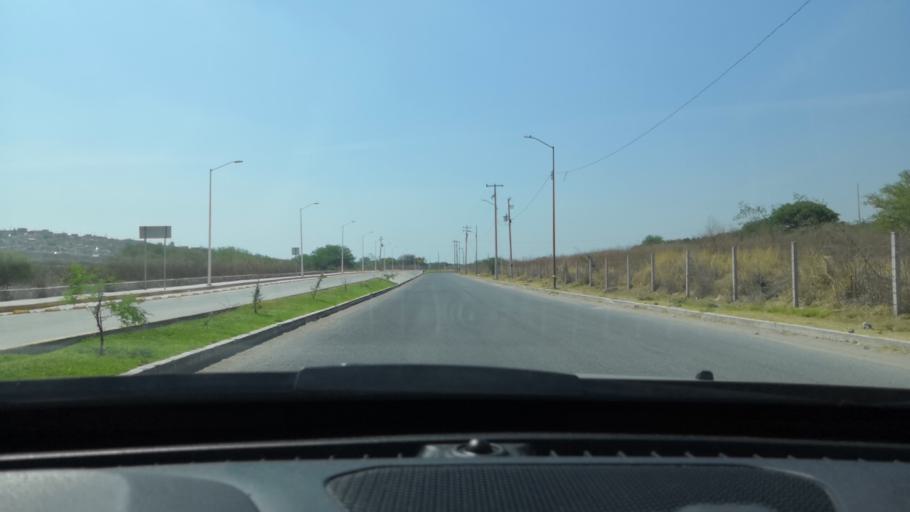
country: MX
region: Guanajuato
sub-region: Purisima del Rincon
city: Potrerillos (Guanajal)
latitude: 21.0574
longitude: -101.8680
